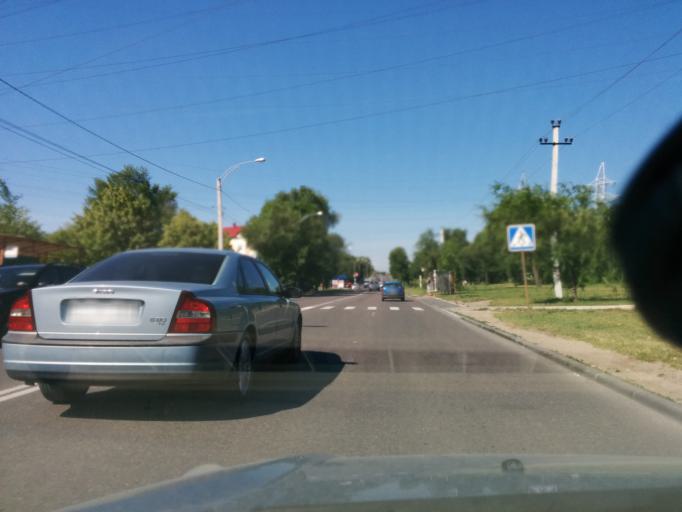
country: MD
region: Chisinau
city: Chisinau
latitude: 47.0321
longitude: 28.8863
